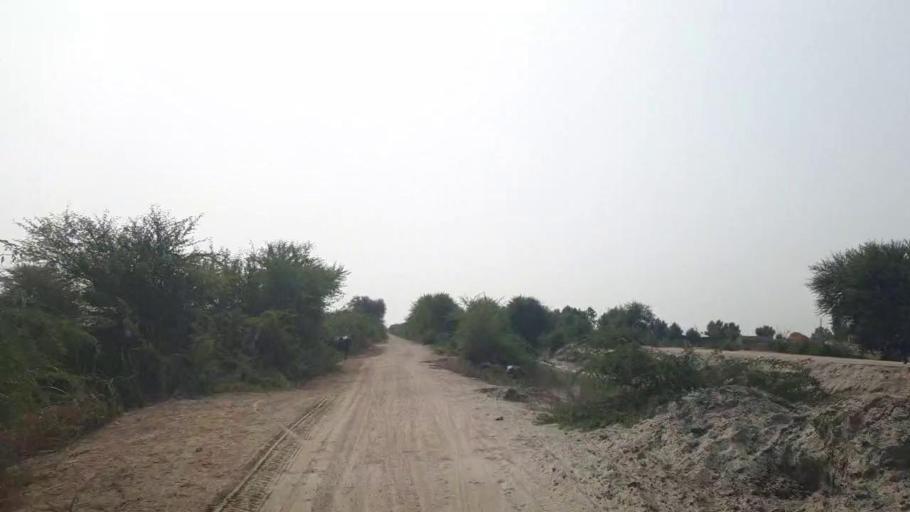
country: PK
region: Sindh
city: Badin
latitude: 24.6118
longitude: 68.7216
